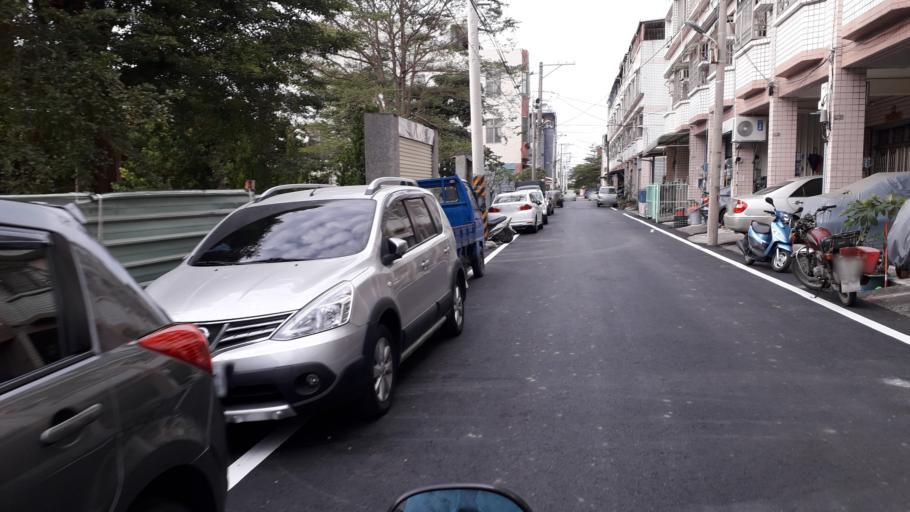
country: TW
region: Taiwan
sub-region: Pingtung
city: Pingtung
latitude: 22.3637
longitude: 120.6030
